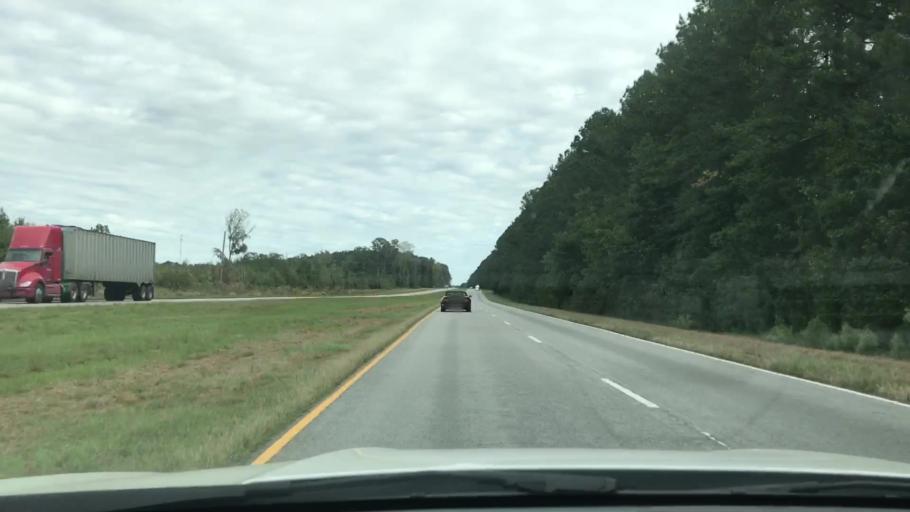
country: US
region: South Carolina
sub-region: Charleston County
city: Ravenel
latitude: 32.7567
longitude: -80.3655
